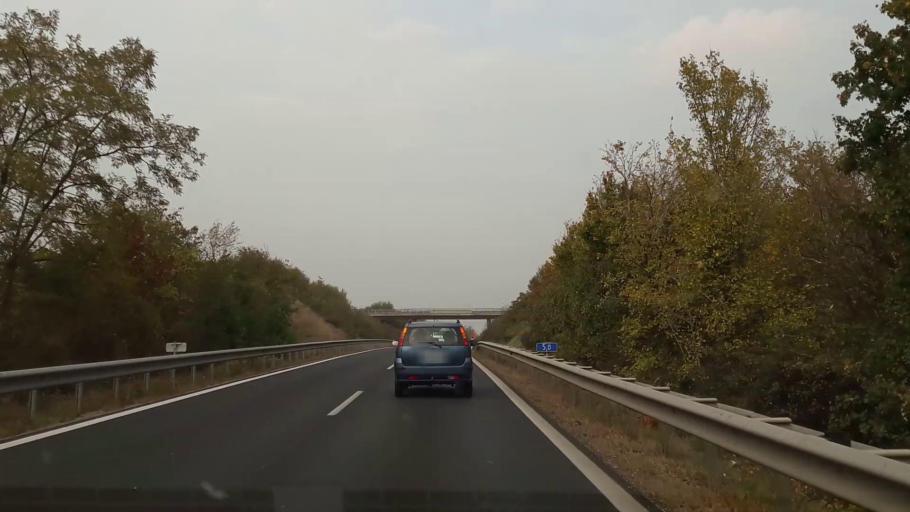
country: AT
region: Burgenland
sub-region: Politischer Bezirk Neusiedl am See
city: Weiden am See
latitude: 47.9137
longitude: 16.8903
